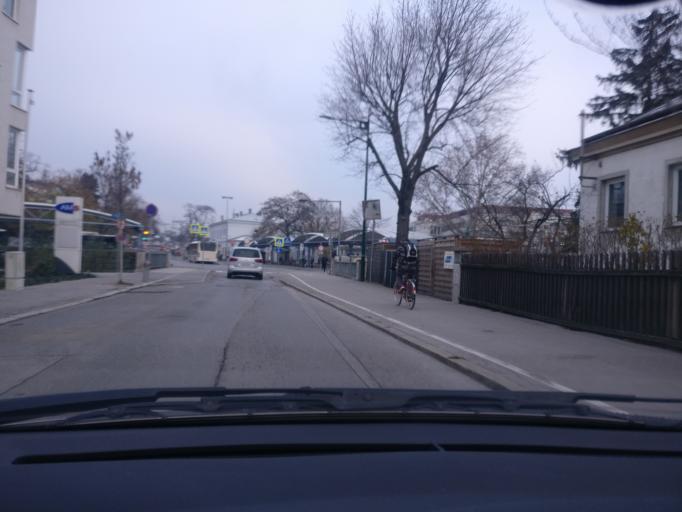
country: AT
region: Lower Austria
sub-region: Politischer Bezirk Modling
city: Modling
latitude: 48.0843
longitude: 16.2958
